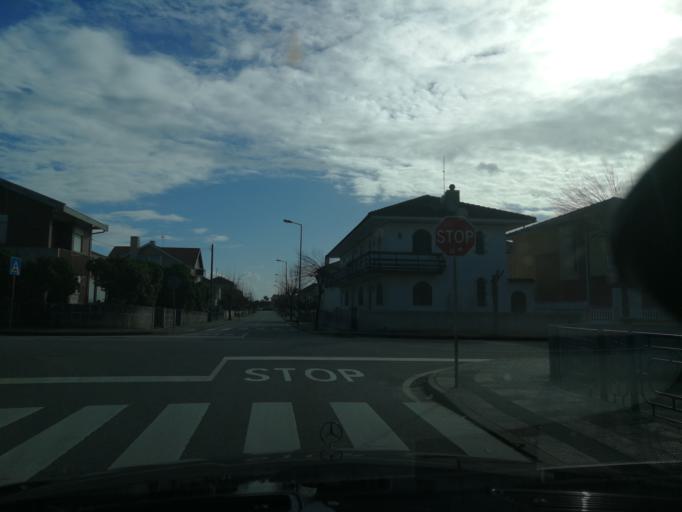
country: PT
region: Aveiro
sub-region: Murtosa
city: Murtosa
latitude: 40.7609
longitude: -8.7086
